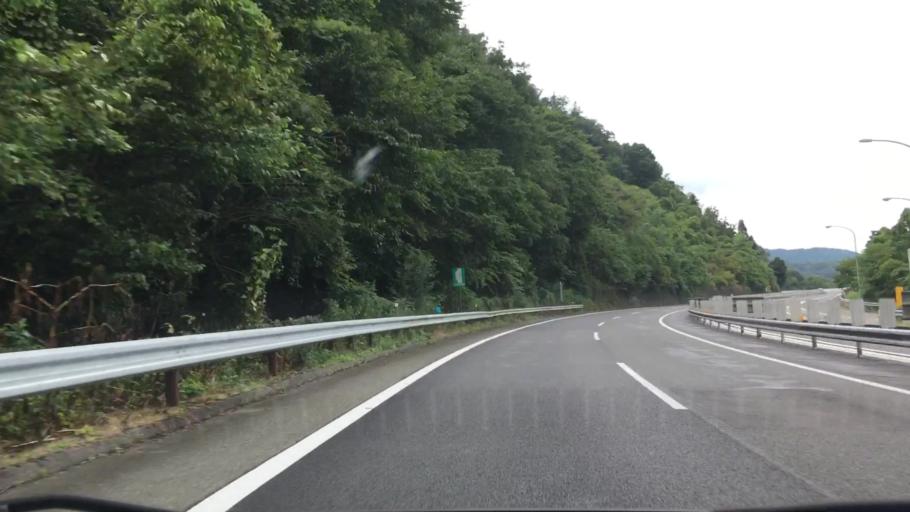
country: JP
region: Hiroshima
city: Shobara
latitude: 34.8944
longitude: 133.2433
